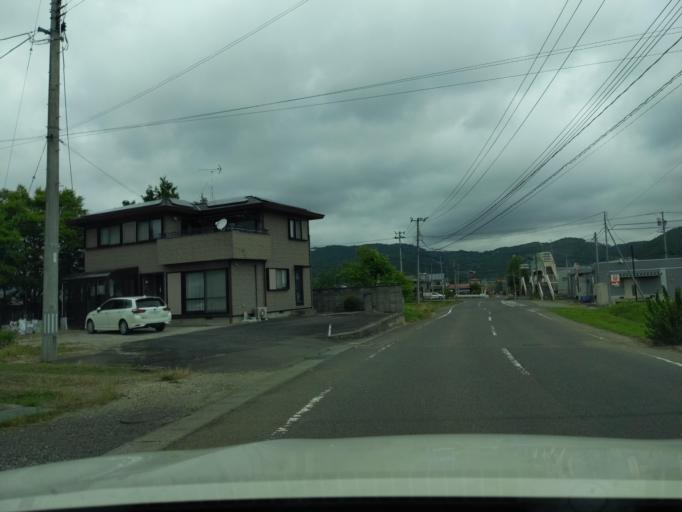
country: JP
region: Fukushima
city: Motomiya
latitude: 37.4712
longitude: 140.3080
